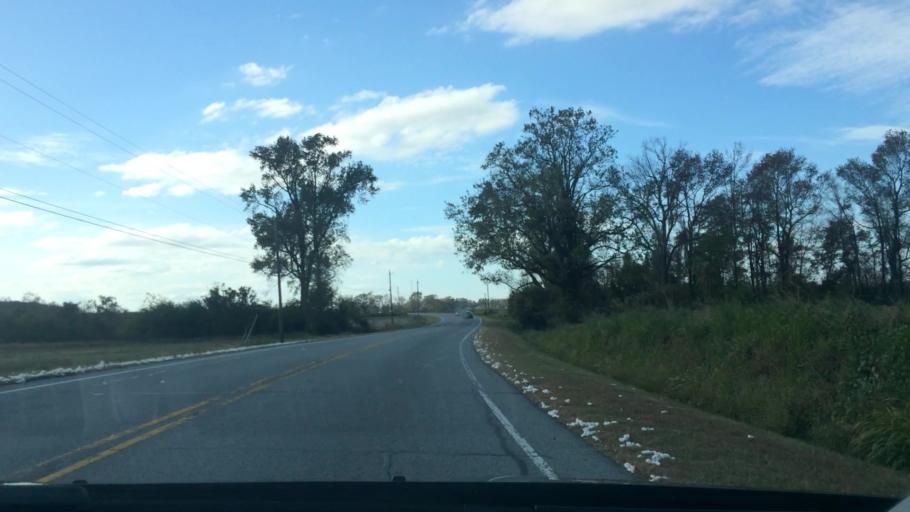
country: US
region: North Carolina
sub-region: Greene County
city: Snow Hill
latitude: 35.4368
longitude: -77.7715
